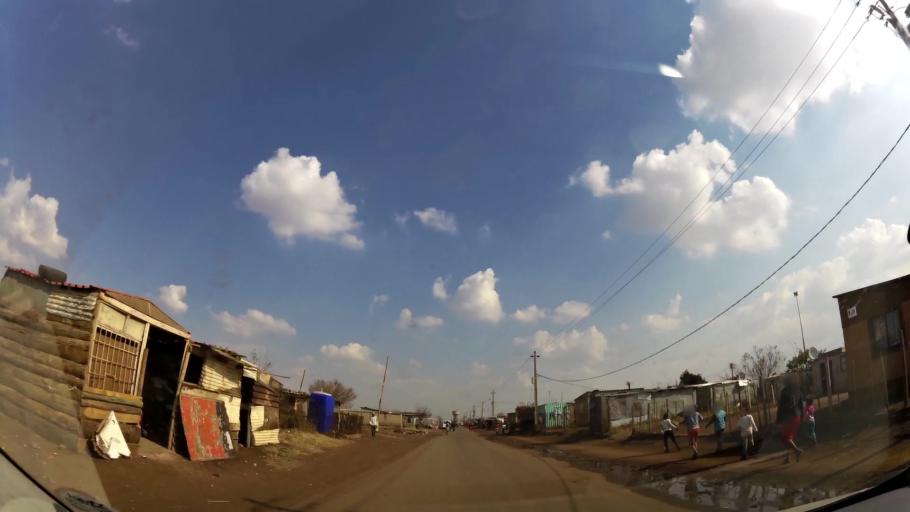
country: ZA
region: Gauteng
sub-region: Ekurhuleni Metropolitan Municipality
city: Germiston
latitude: -26.3365
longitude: 28.1382
